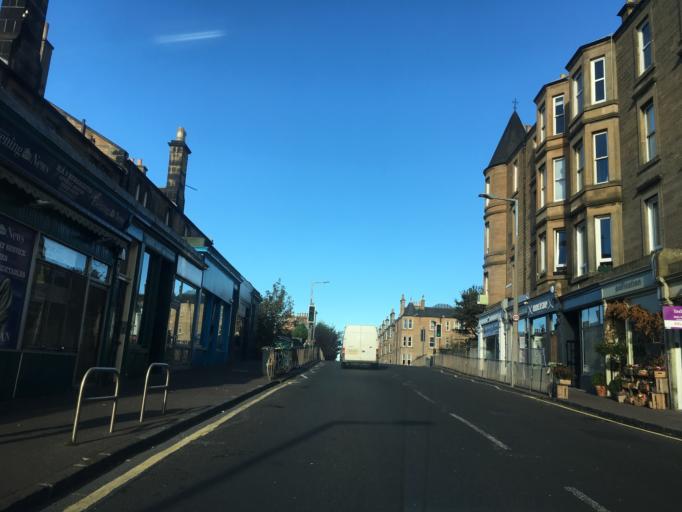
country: GB
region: Scotland
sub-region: Edinburgh
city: Colinton
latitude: 55.9333
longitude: -3.2296
